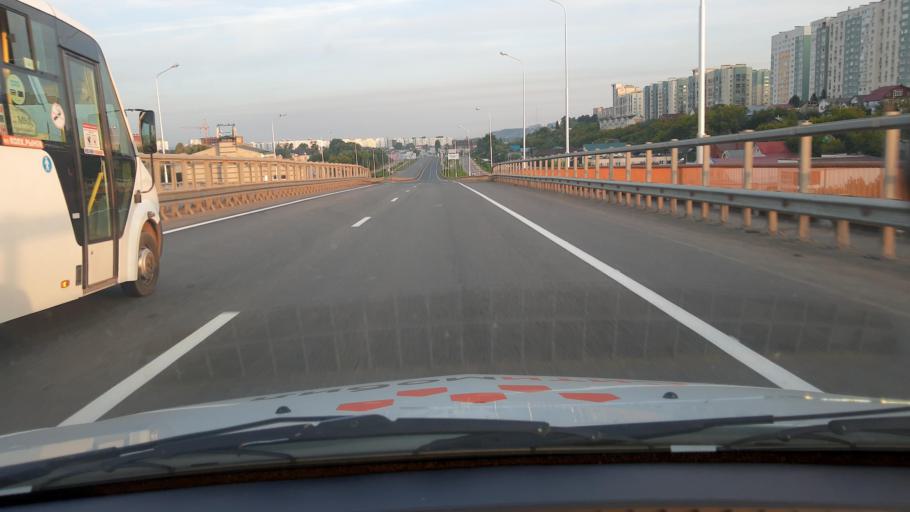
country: RU
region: Bashkortostan
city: Ufa
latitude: 54.6849
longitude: 55.9984
